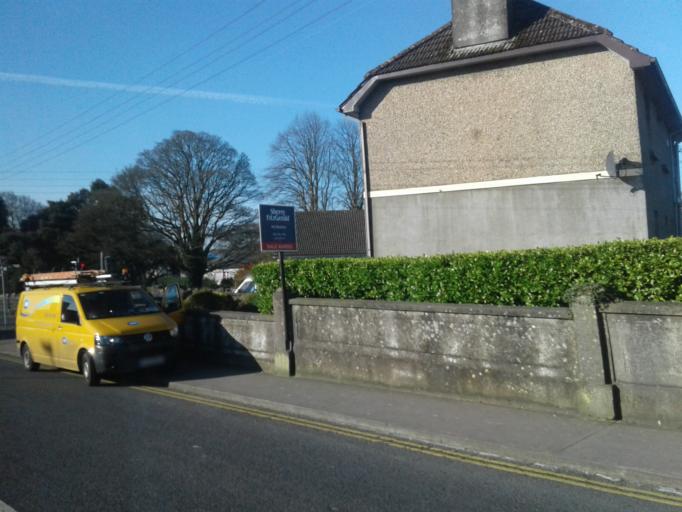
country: IE
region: Munster
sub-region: An Clar
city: Ennis
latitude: 52.8363
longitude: -8.9829
